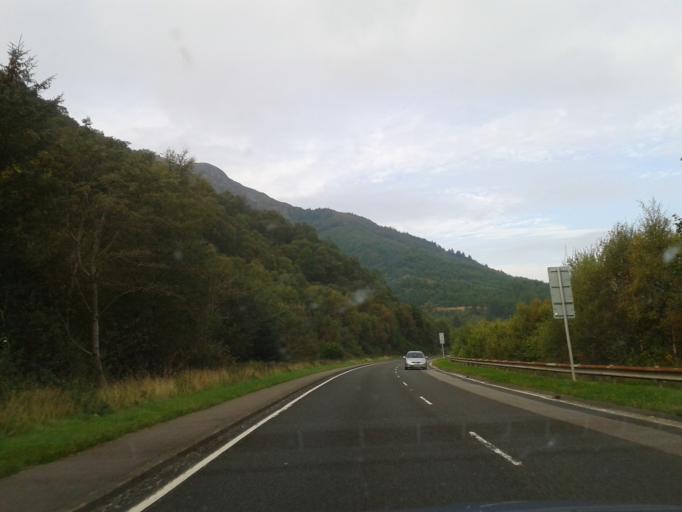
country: GB
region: Scotland
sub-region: Highland
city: Fort William
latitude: 56.6768
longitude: -5.1475
